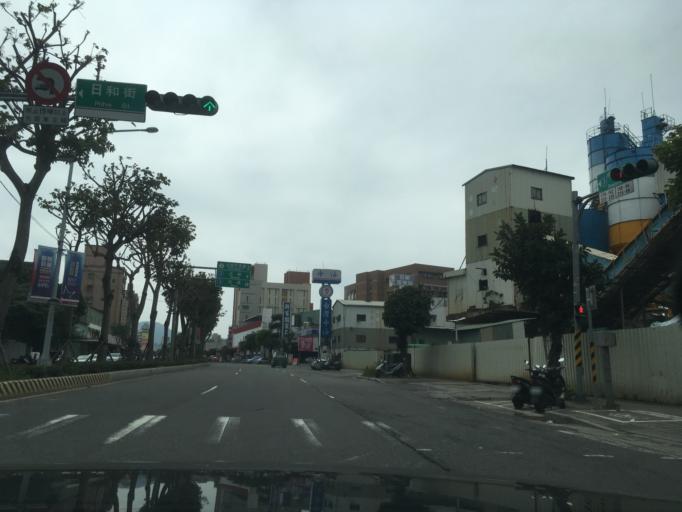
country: TW
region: Taipei
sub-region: Taipei
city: Banqiao
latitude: 24.9844
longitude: 121.4424
